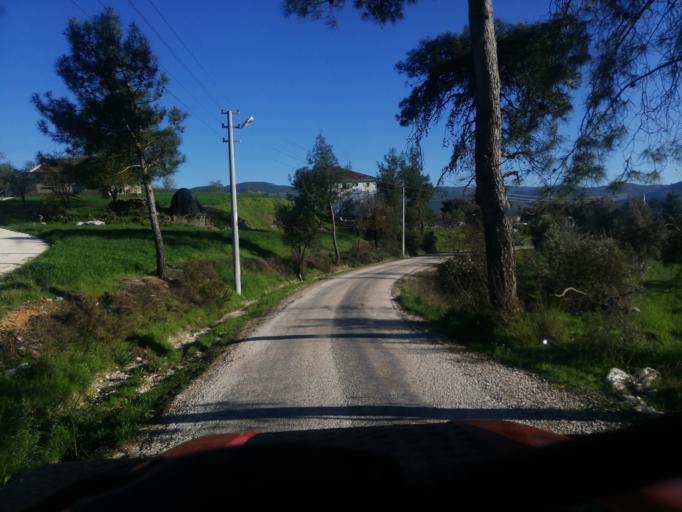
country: TR
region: Antalya
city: Kas
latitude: 36.2922
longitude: 29.7063
